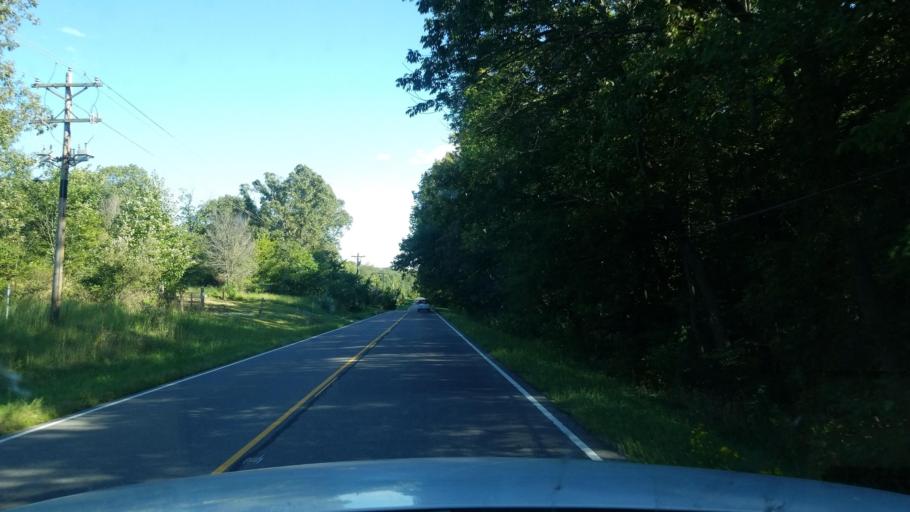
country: US
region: Illinois
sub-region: Saline County
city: Harrisburg
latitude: 37.6154
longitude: -88.4677
